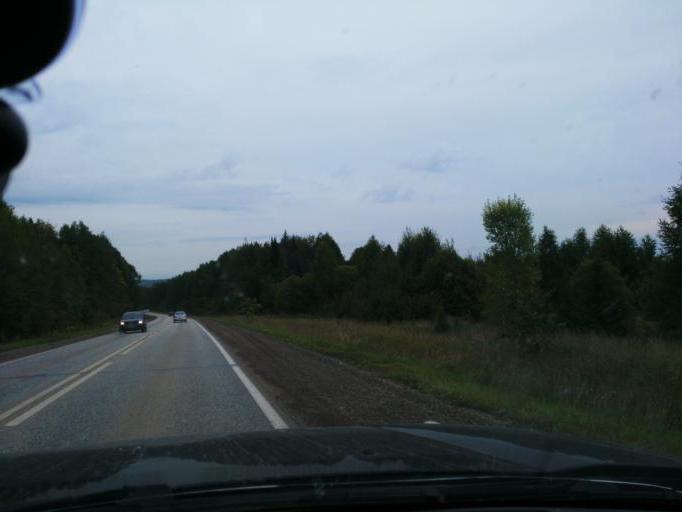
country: RU
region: Perm
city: Chernushka
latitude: 56.5909
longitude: 56.1541
